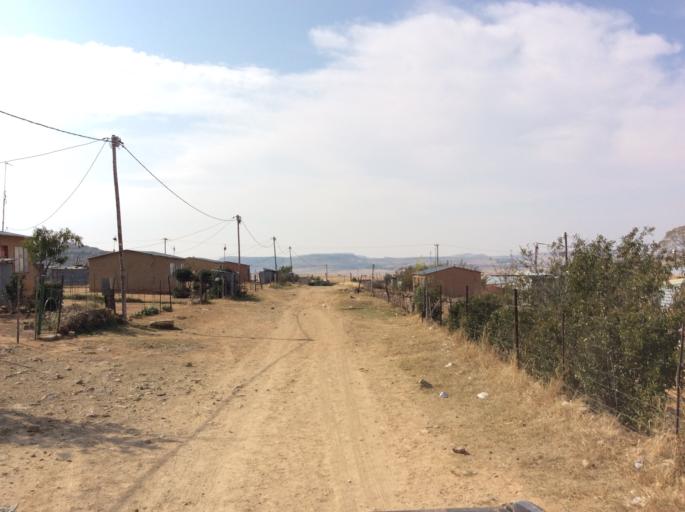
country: ZA
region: Orange Free State
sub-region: Xhariep District Municipality
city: Dewetsdorp
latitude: -29.5981
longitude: 26.6792
